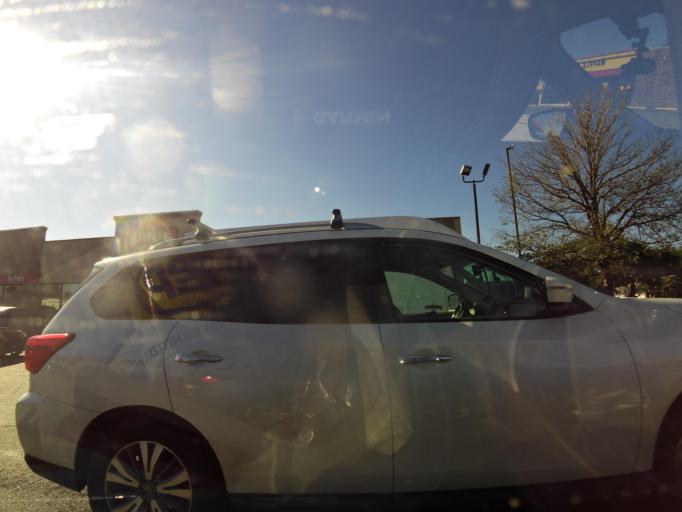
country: US
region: Florida
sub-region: Jackson County
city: Marianna
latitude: 30.7257
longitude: -85.1865
